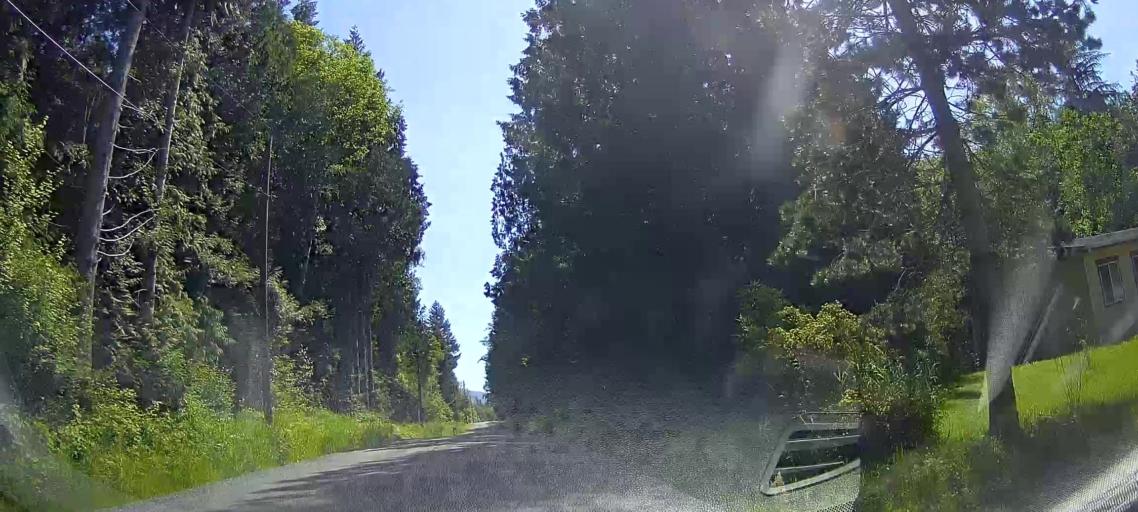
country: US
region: Washington
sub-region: Skagit County
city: Sedro-Woolley
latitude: 48.5545
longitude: -122.2733
